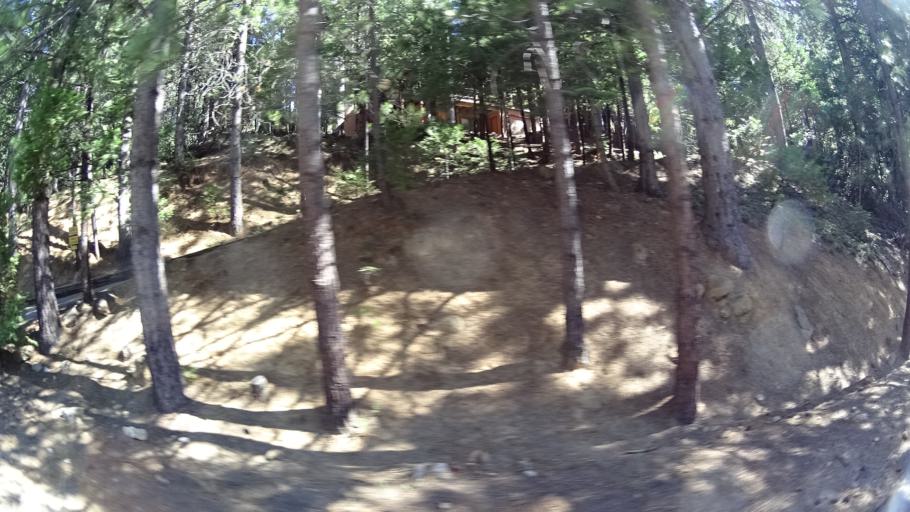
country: US
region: California
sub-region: Calaveras County
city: Arnold
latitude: 38.2940
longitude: -120.2687
